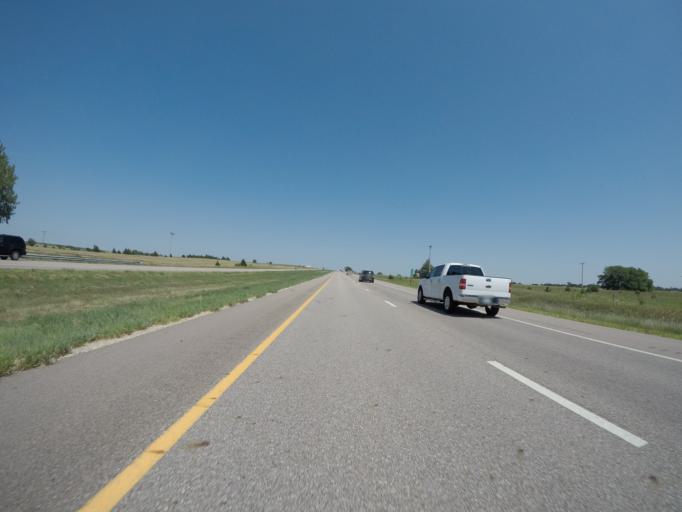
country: US
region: Kansas
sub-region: Russell County
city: Russell
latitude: 38.8565
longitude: -98.5962
